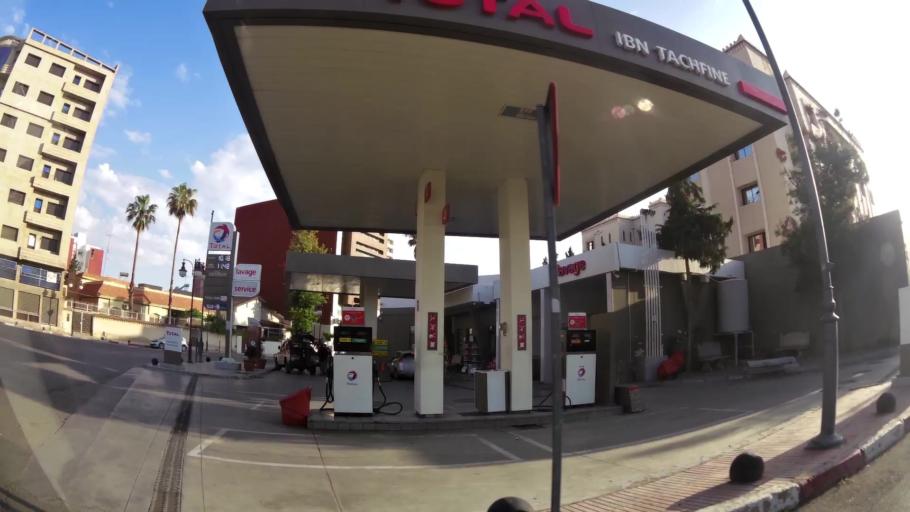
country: MA
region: Oriental
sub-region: Oujda-Angad
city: Oujda
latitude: 34.6765
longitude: -1.9221
